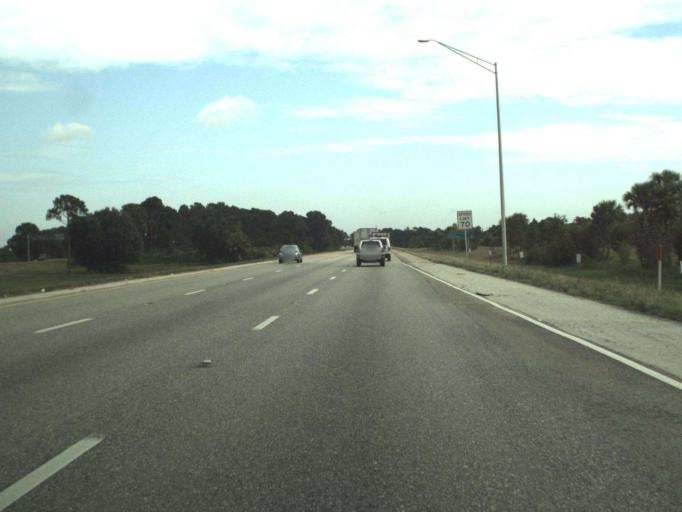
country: US
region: Florida
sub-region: Saint Lucie County
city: Port Saint Lucie
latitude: 27.2161
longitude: -80.4002
